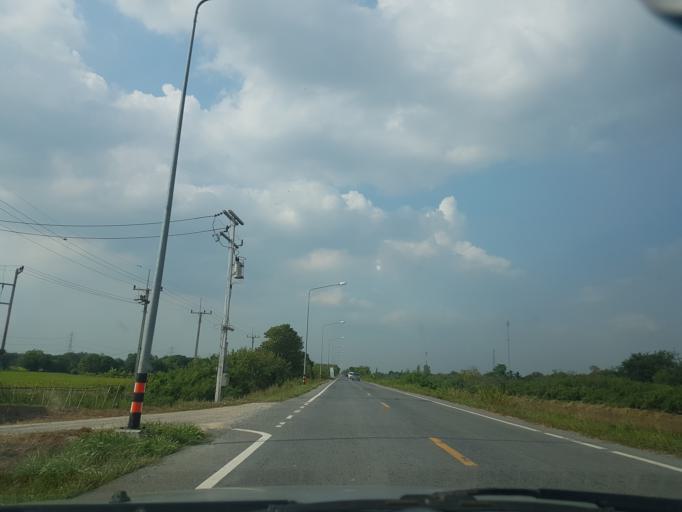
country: TH
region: Phra Nakhon Si Ayutthaya
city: Phachi
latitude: 14.4623
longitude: 100.7536
